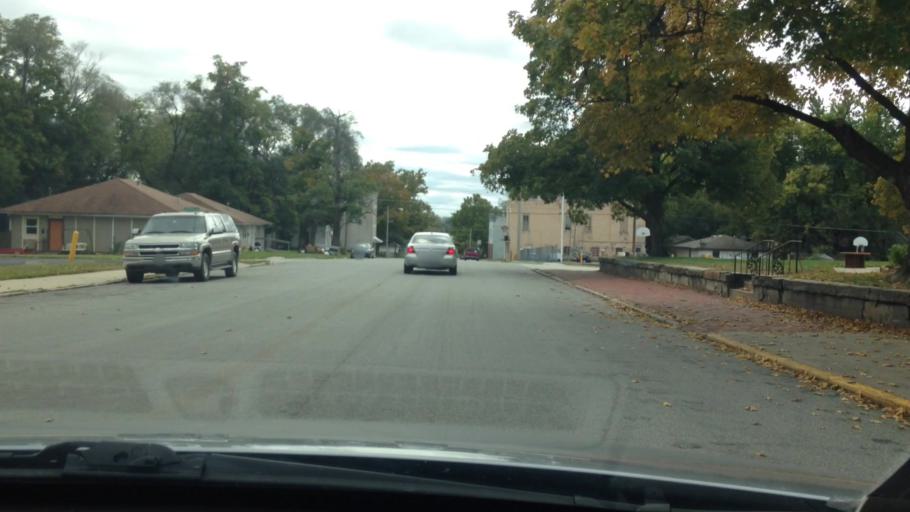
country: US
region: Kansas
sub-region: Leavenworth County
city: Leavenworth
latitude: 39.3246
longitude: -94.9168
